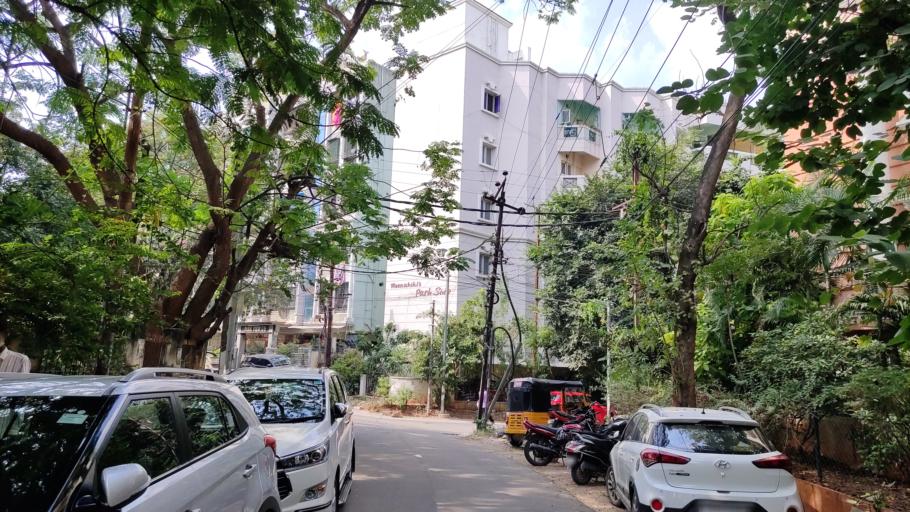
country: IN
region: Telangana
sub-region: Hyderabad
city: Hyderabad
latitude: 17.4305
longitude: 78.4428
